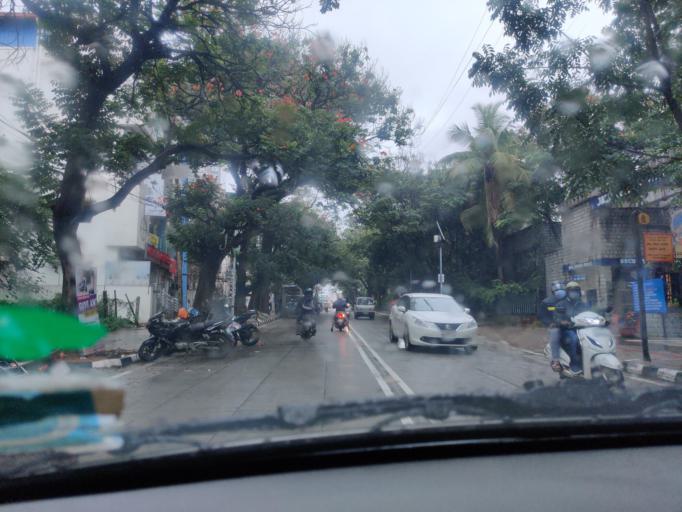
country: IN
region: Karnataka
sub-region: Bangalore Urban
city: Bangalore
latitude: 13.0233
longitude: 77.6356
